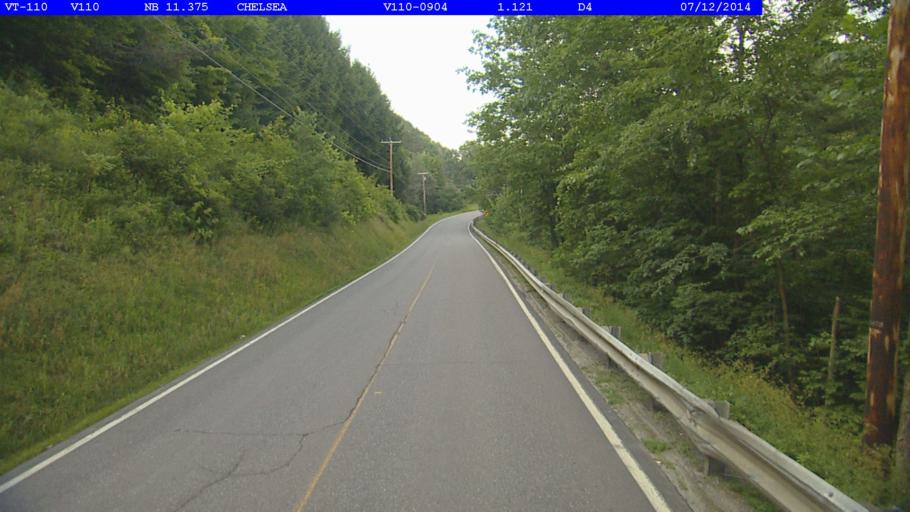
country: US
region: Vermont
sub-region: Orange County
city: Chelsea
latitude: 43.9665
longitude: -72.4617
